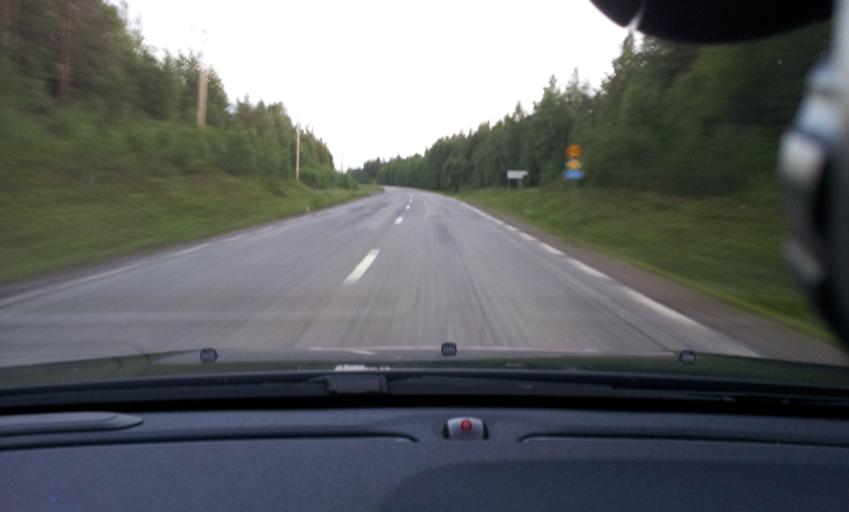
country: SE
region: Jaemtland
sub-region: Ragunda Kommun
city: Hammarstrand
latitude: 63.0110
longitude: 16.1203
